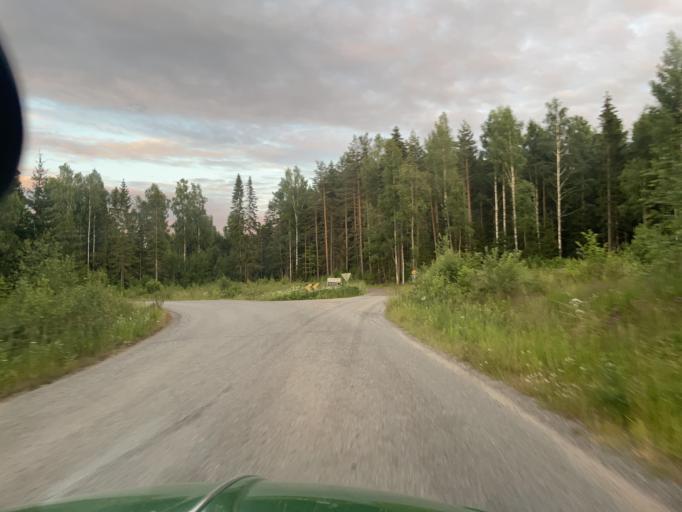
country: FI
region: Uusimaa
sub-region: Helsinki
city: Lohja
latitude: 60.2162
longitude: 24.0876
